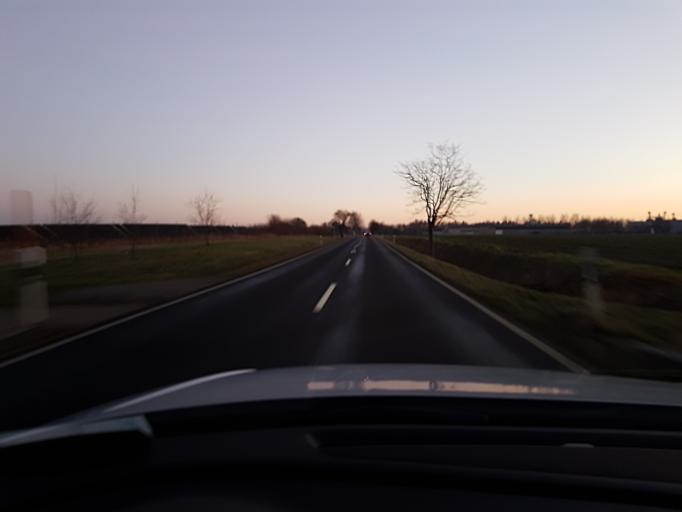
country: DE
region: Mecklenburg-Vorpommern
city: Gingst
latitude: 54.4723
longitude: 13.2949
